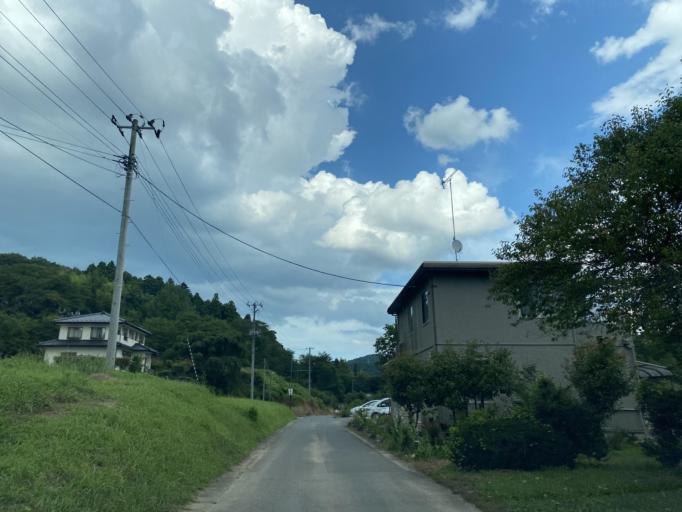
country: JP
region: Fukushima
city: Koriyama
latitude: 37.3736
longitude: 140.4377
